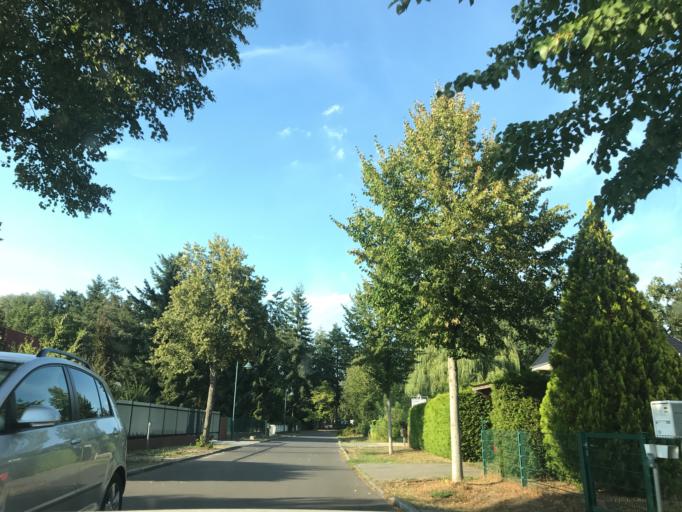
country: DE
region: Brandenburg
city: Potsdam
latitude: 52.4439
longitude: 13.0304
